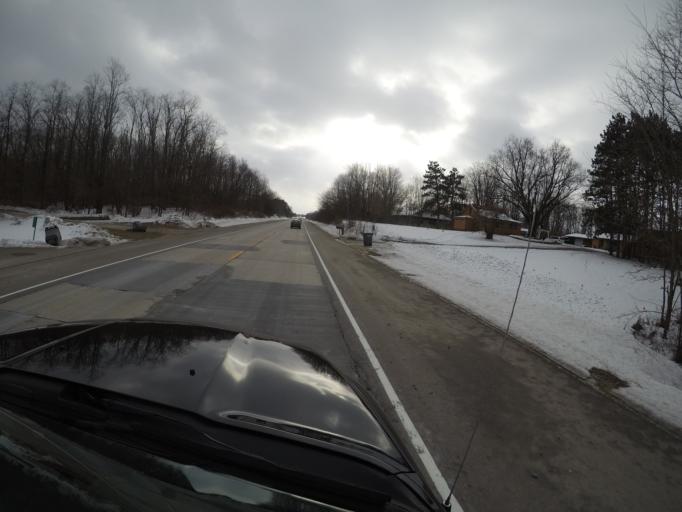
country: US
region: Wisconsin
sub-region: Trempealeau County
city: Galesville
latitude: 44.0401
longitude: -91.2907
